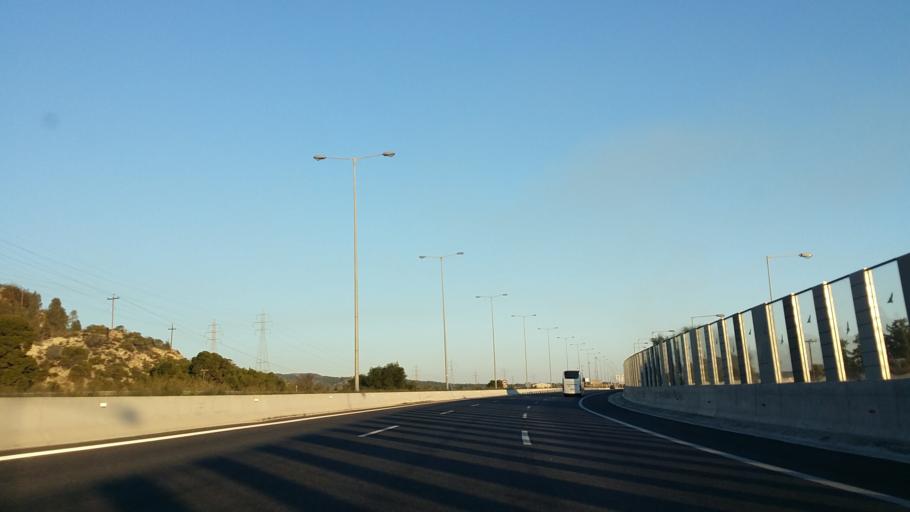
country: GR
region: Peloponnese
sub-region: Nomos Korinthias
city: Isthmia
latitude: 37.9259
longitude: 23.0180
